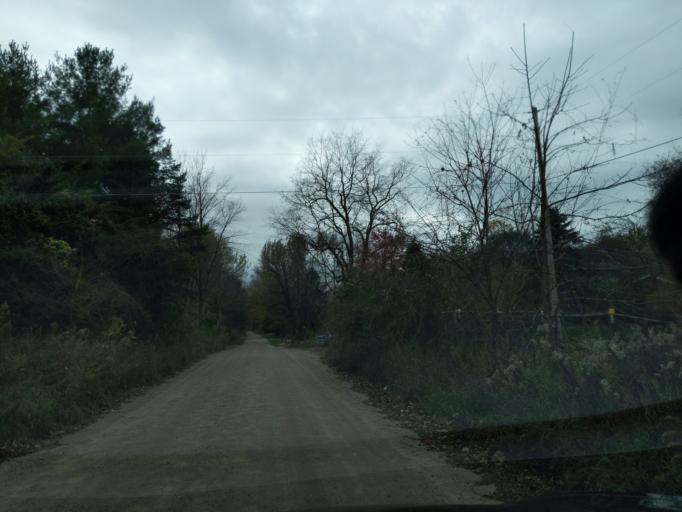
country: US
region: Michigan
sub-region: Eaton County
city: Eaton Rapids
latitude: 42.5517
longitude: -84.6138
